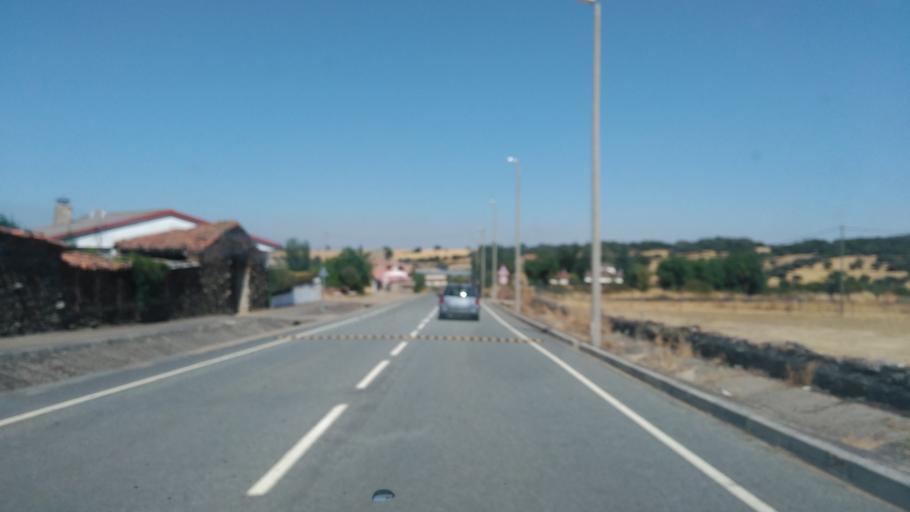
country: ES
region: Castille and Leon
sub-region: Provincia de Salamanca
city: Aldeanueva de la Sierra
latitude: 40.6147
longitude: -6.0981
